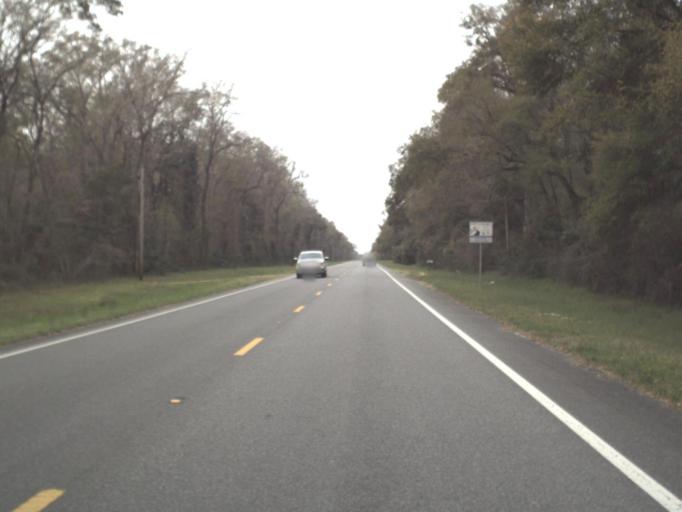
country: US
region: Florida
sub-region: Wakulla County
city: Crawfordville
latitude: 30.1498
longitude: -84.2810
